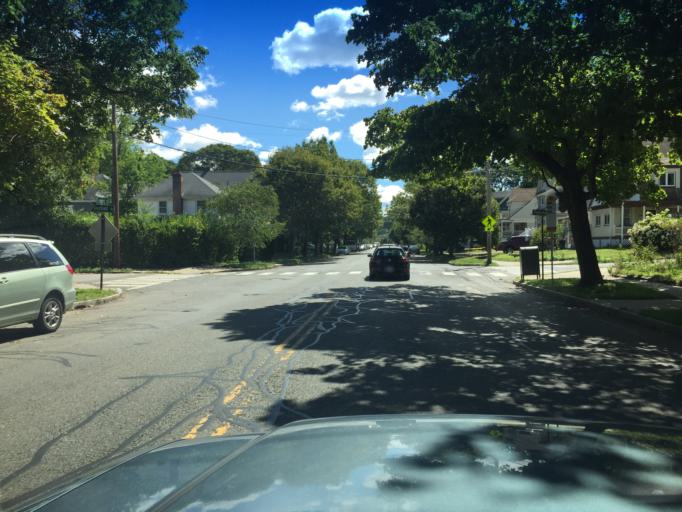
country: US
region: Massachusetts
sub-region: Middlesex County
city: Watertown
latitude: 42.3530
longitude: -71.1770
